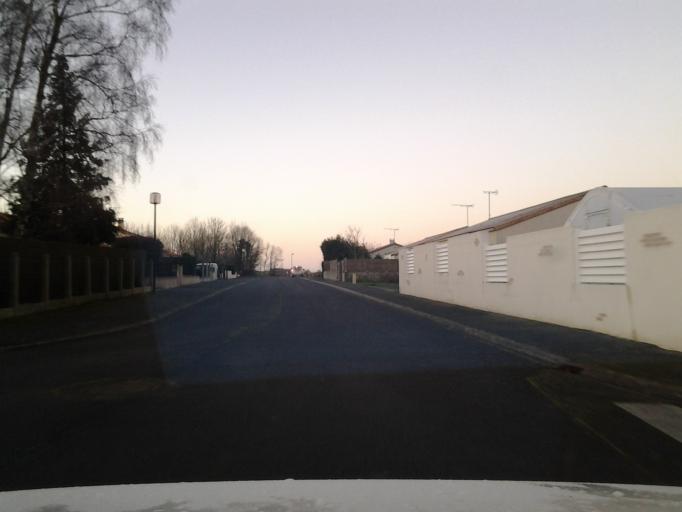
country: FR
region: Pays de la Loire
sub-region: Departement de la Vendee
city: Les Epesses
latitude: 46.8783
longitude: -0.9033
